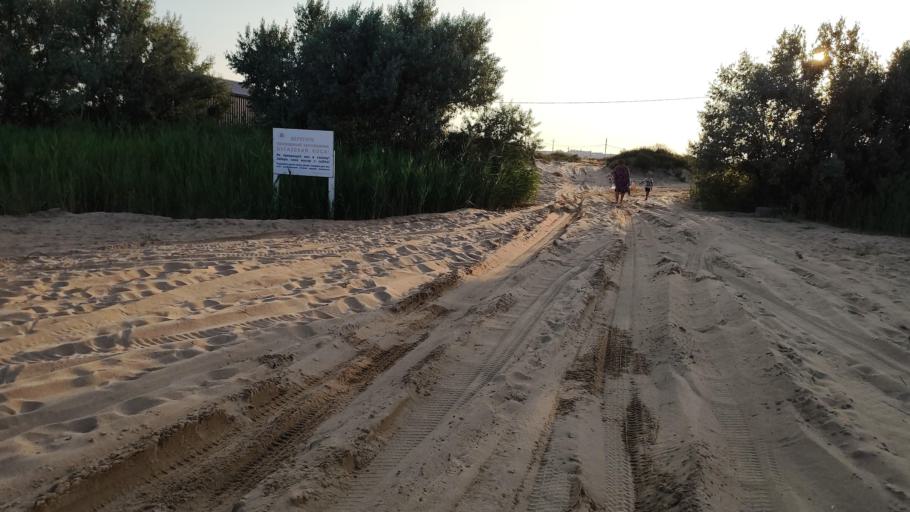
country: RU
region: Krasnodarskiy
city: Blagovetschenskaya
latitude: 45.0667
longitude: 37.0395
